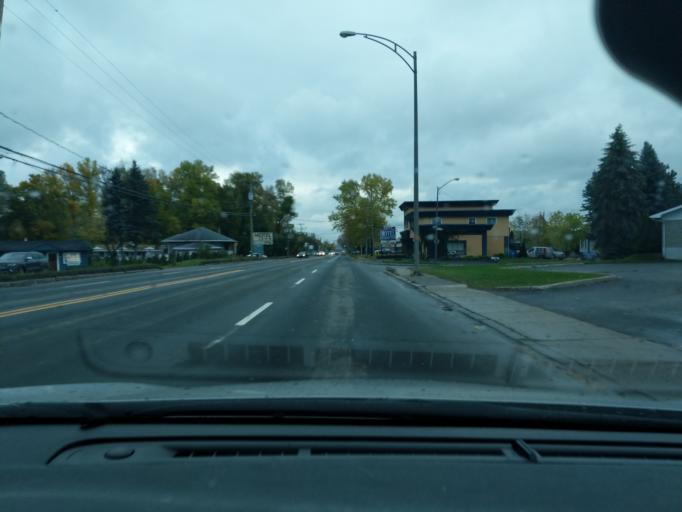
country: CA
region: Quebec
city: L'Ancienne-Lorette
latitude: 46.8062
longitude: -71.3088
